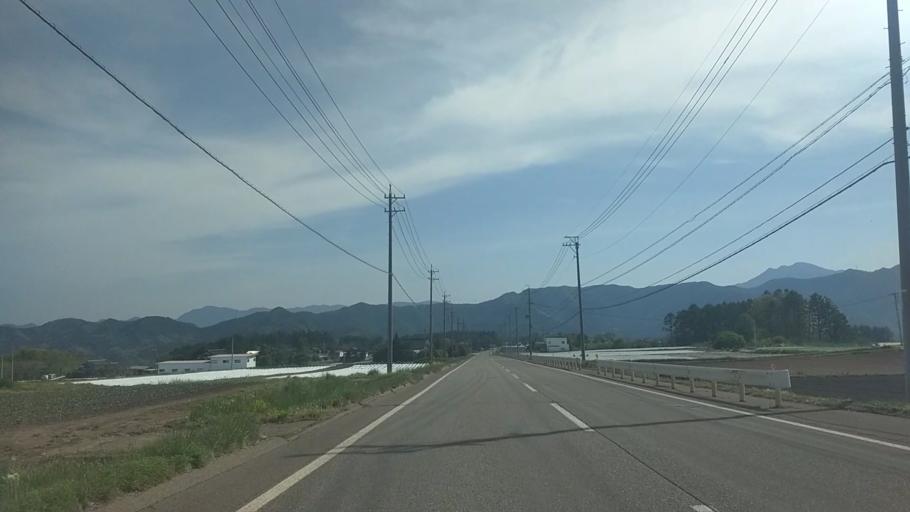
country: JP
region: Nagano
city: Saku
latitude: 35.9916
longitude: 138.4912
